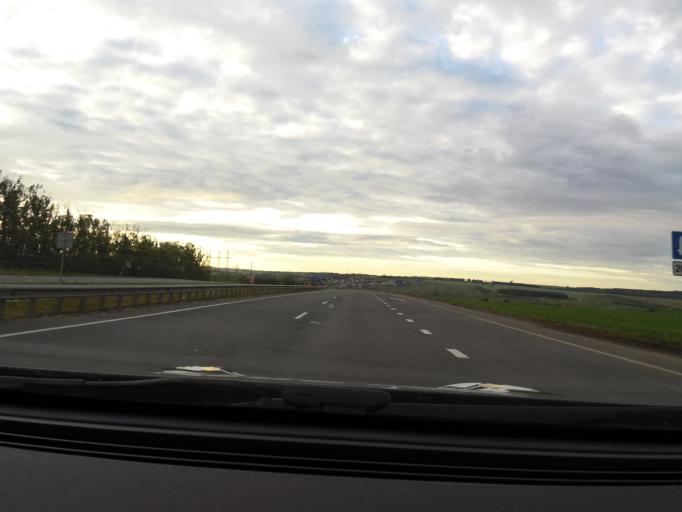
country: RU
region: Chuvashia
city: Kugesi
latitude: 55.9657
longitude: 47.3703
